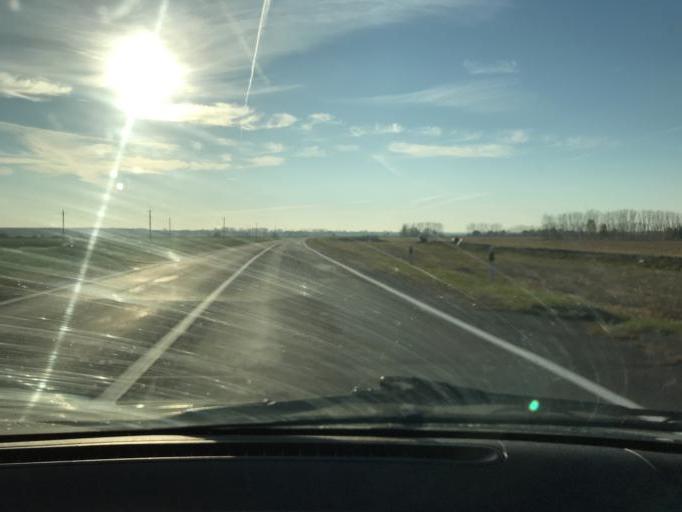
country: BY
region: Brest
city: Antopal'
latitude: 52.2111
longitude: 24.6422
